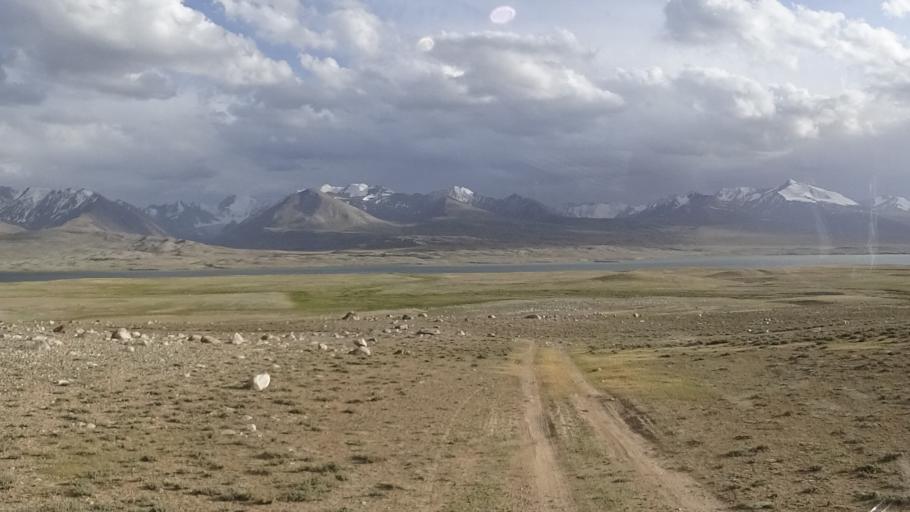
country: TJ
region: Gorno-Badakhshan
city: Murghob
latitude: 37.4650
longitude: 73.6131
